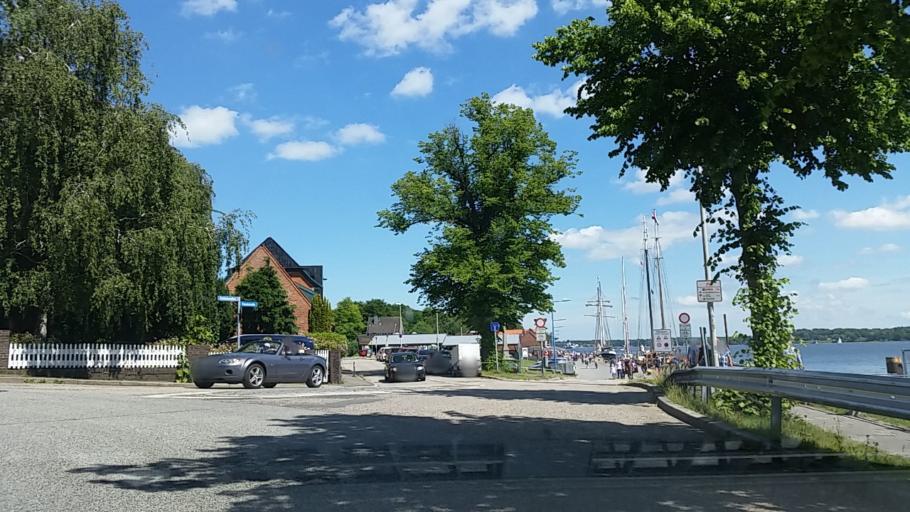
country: DE
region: Schleswig-Holstein
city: Altenholz
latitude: 54.3690
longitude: 10.1481
